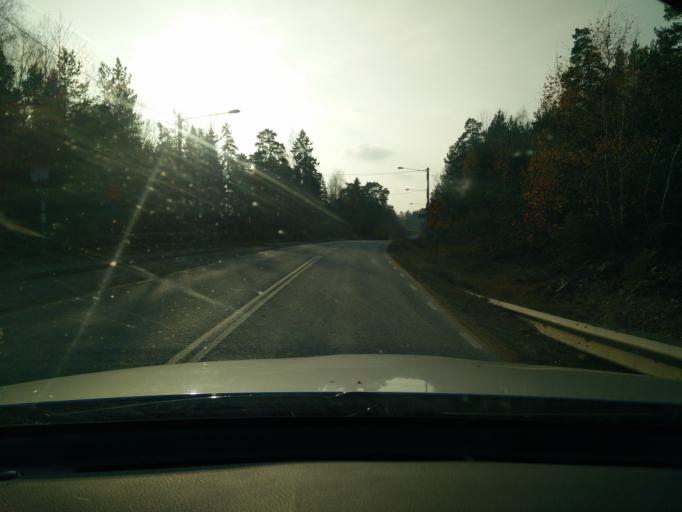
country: SE
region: Stockholm
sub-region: Sollentuna Kommun
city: Sollentuna
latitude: 59.4630
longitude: 17.9789
